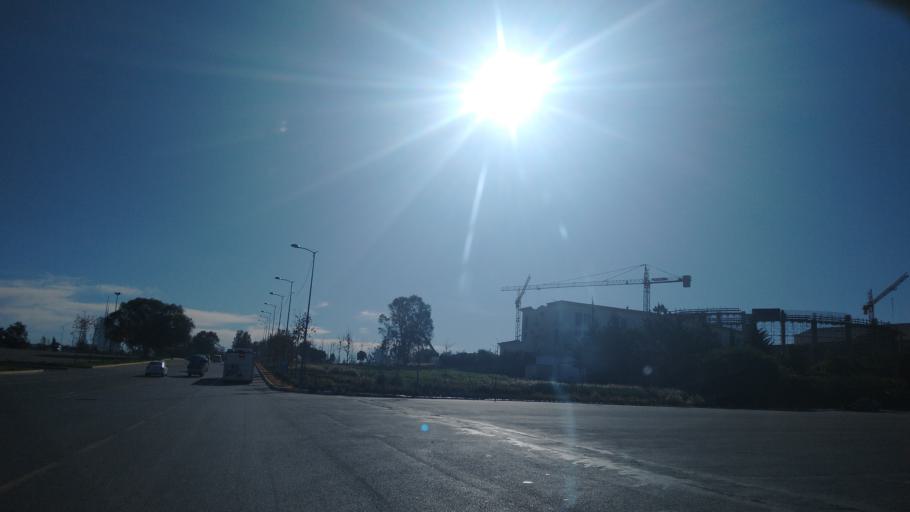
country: MA
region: Rabat-Sale-Zemmour-Zaer
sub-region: Skhirate-Temara
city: Temara
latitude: 33.9655
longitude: -6.8870
